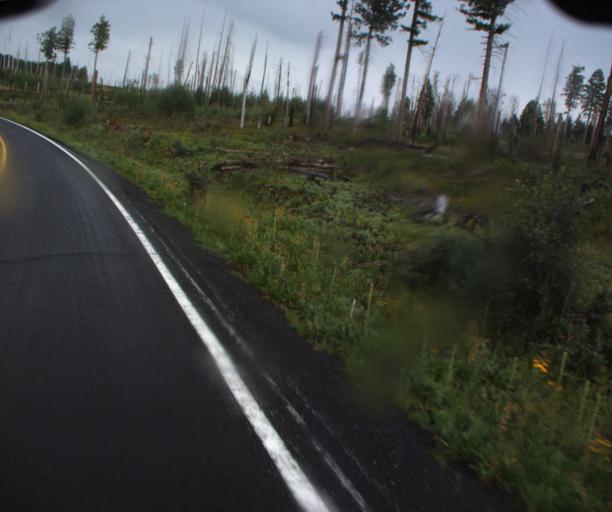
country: US
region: Arizona
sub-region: Greenlee County
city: Morenci
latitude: 33.5869
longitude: -109.3514
